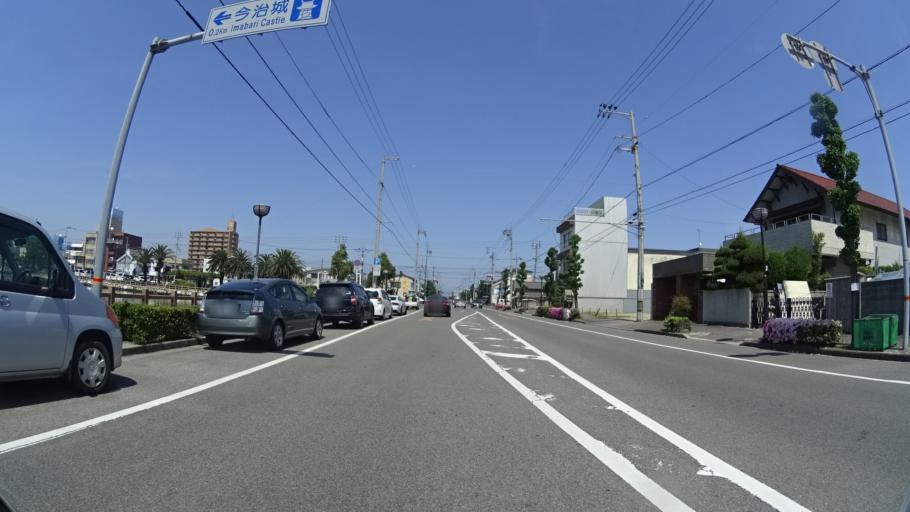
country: JP
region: Ehime
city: Saijo
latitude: 34.0628
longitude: 133.0084
